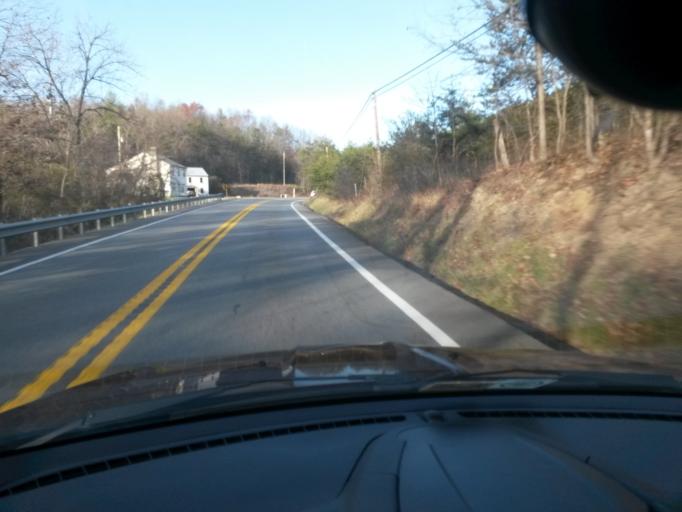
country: US
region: Virginia
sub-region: Alleghany County
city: Clifton Forge
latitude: 37.7185
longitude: -79.8073
